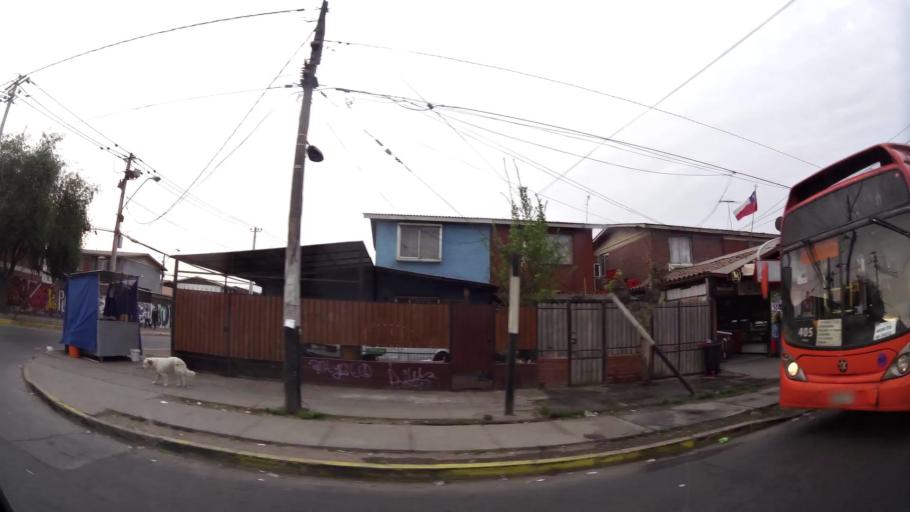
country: CL
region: Santiago Metropolitan
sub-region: Provincia de Santiago
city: Lo Prado
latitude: -33.5196
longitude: -70.7943
